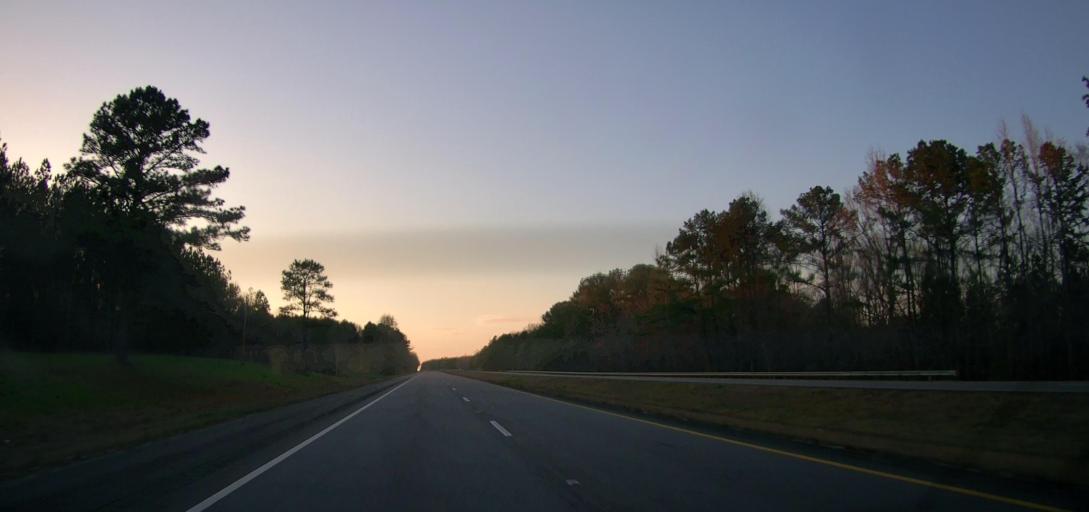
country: US
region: Alabama
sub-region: Coosa County
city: Goodwater
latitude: 33.0081
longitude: -86.0904
